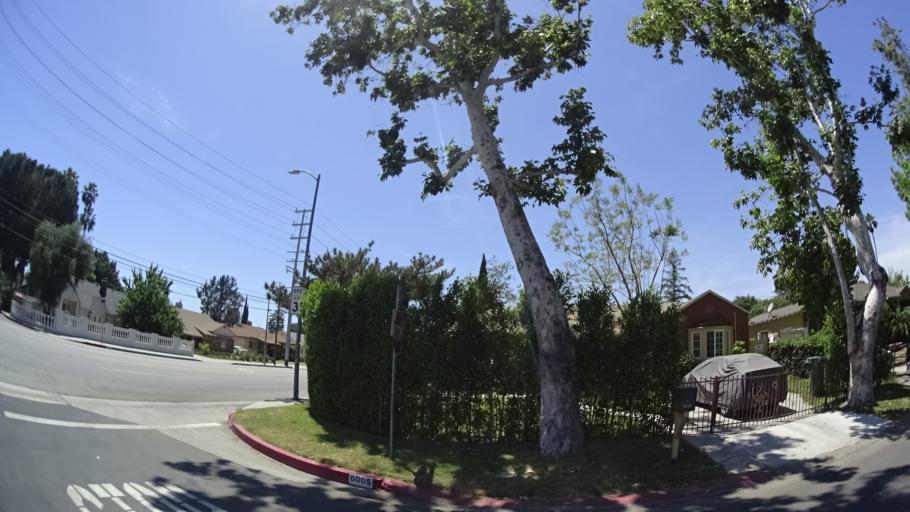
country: US
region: California
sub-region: Los Angeles County
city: North Hollywood
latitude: 34.1796
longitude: -118.3888
